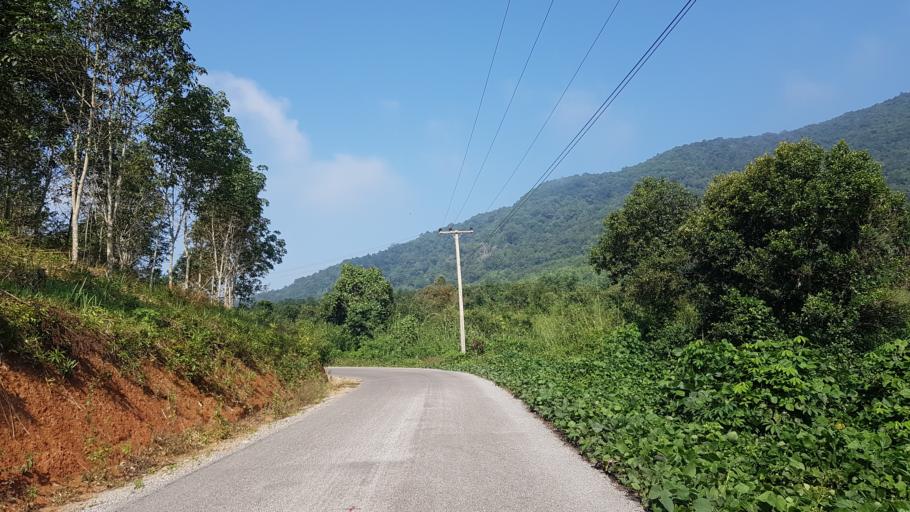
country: LA
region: Oudomxai
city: Muang Xay
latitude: 20.7125
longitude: 102.0715
